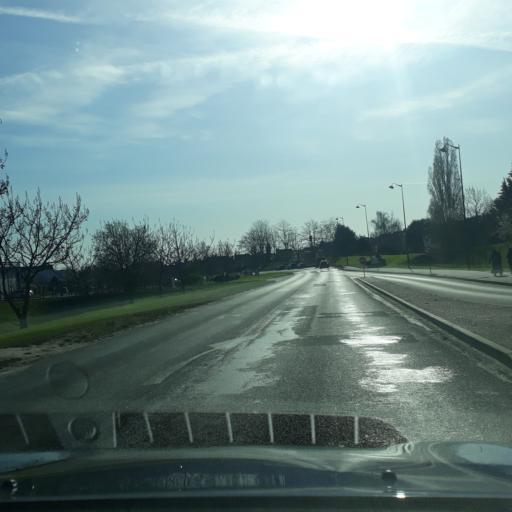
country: FR
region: Ile-de-France
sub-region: Departement de l'Essonne
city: Etampes
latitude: 48.4409
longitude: 2.1422
